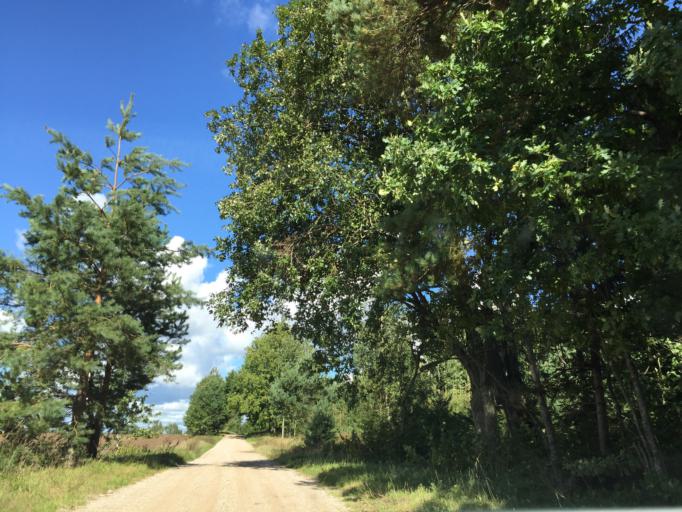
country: LV
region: Kuldigas Rajons
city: Kuldiga
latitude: 56.9696
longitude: 21.9069
